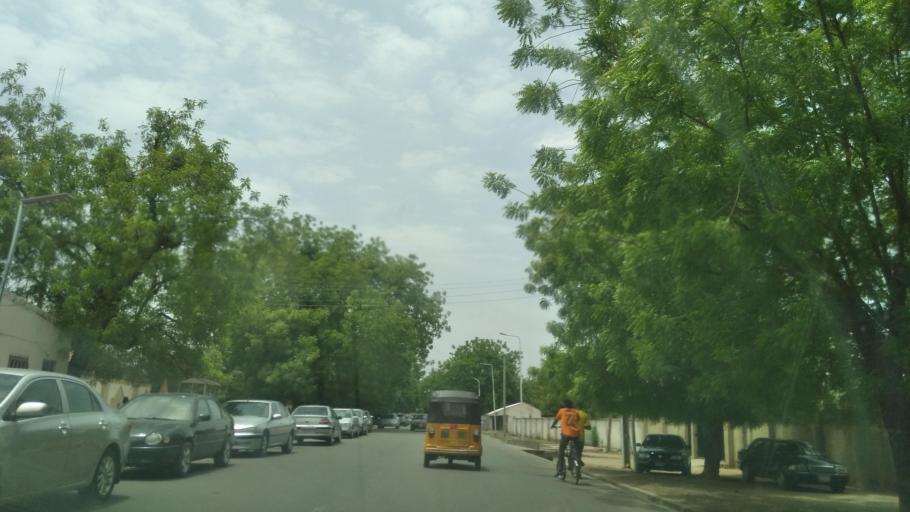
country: NG
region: Borno
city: Maiduguri
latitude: 11.8072
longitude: 13.1588
